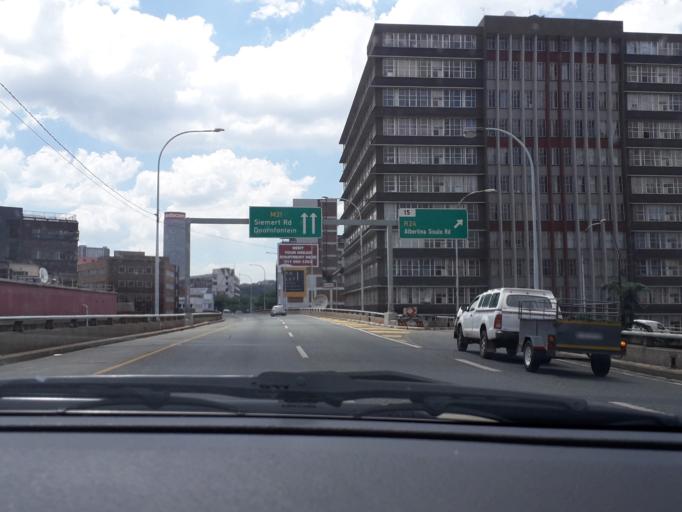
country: ZA
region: Gauteng
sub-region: City of Johannesburg Metropolitan Municipality
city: Johannesburg
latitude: -26.2035
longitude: 28.0547
